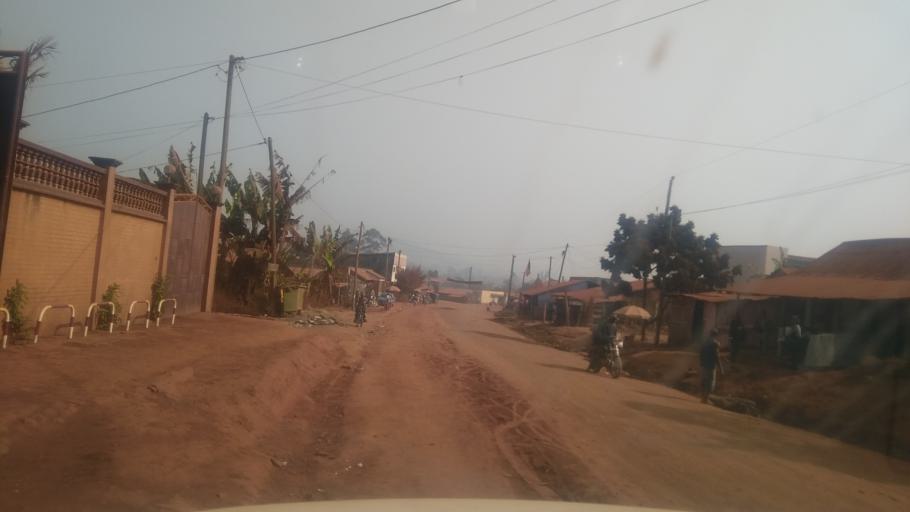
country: CM
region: West
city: Bafoussam
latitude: 5.5093
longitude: 10.4027
